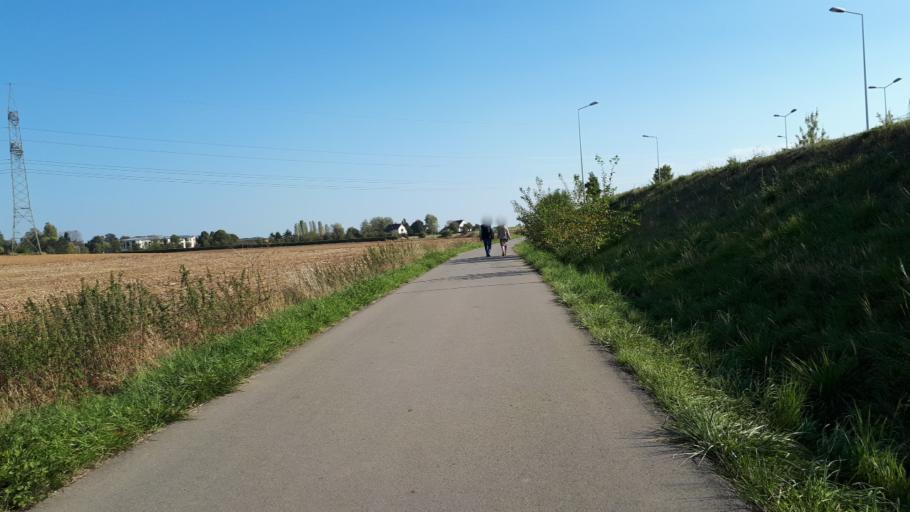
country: LU
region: Luxembourg
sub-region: Canton de Luxembourg
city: Bertrange
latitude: 49.6187
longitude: 6.0381
